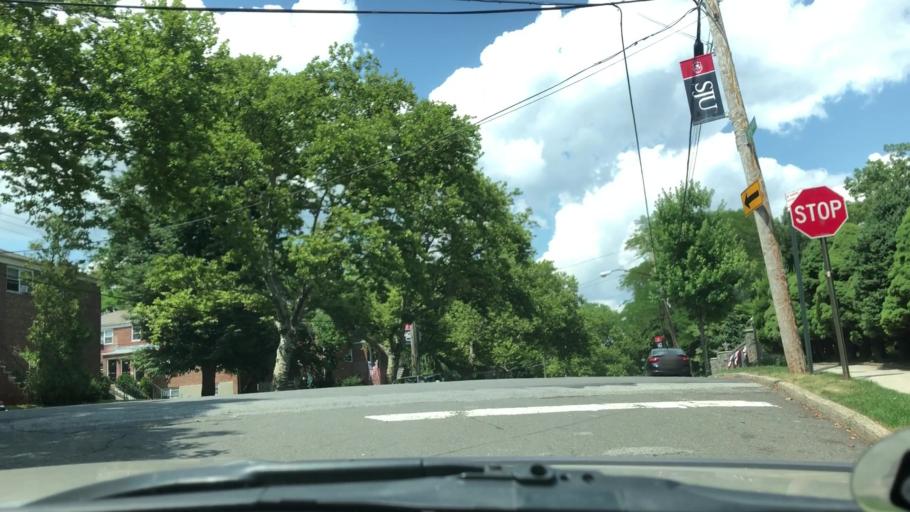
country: US
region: New Jersey
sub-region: Hudson County
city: Bayonne
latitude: 40.6185
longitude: -74.0907
